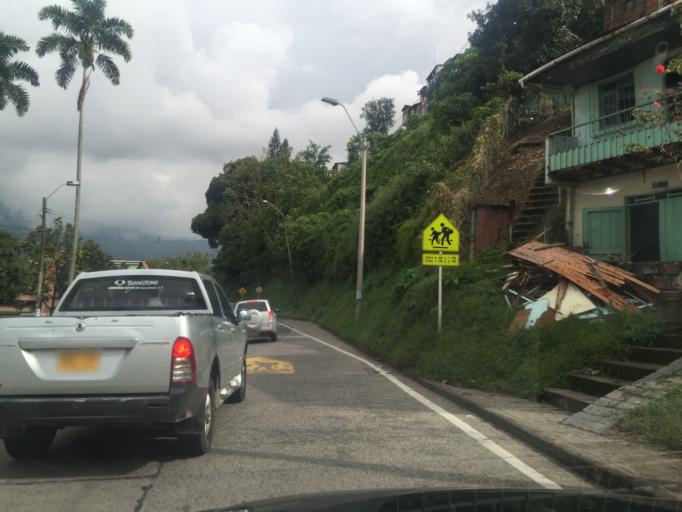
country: CO
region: Risaralda
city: Pereira
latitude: 4.7962
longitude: -75.6947
